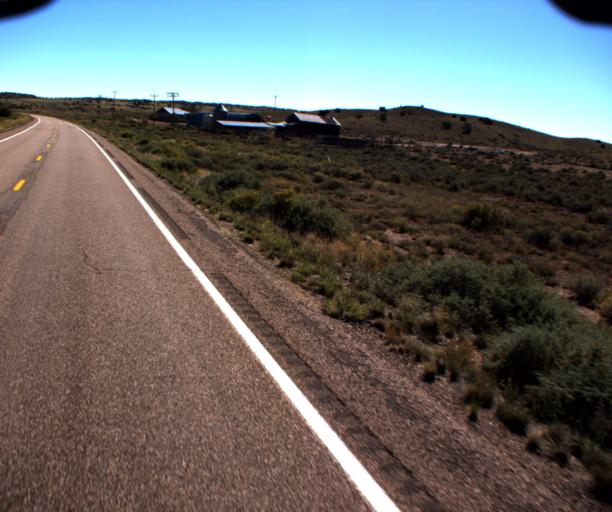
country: US
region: Arizona
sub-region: Apache County
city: Saint Johns
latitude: 34.5857
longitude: -109.5796
